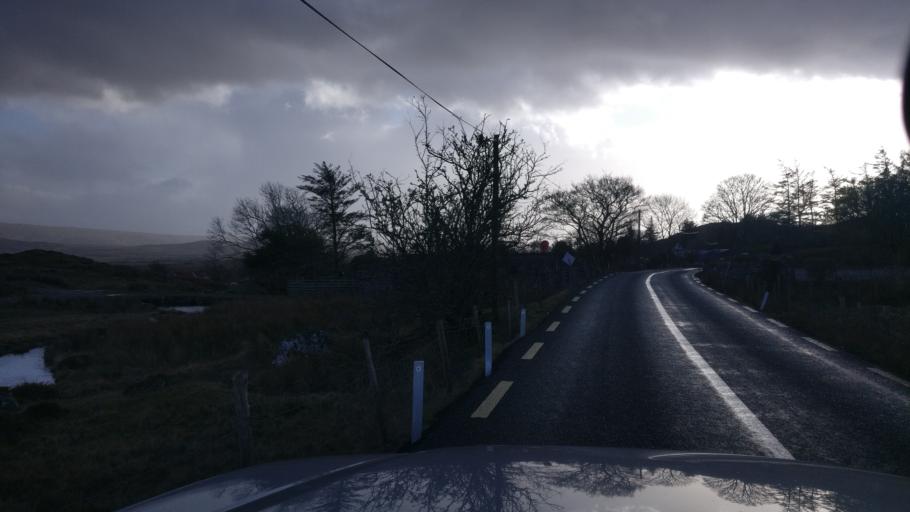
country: IE
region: Connaught
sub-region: County Galway
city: Clifden
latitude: 53.4255
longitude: -9.7720
